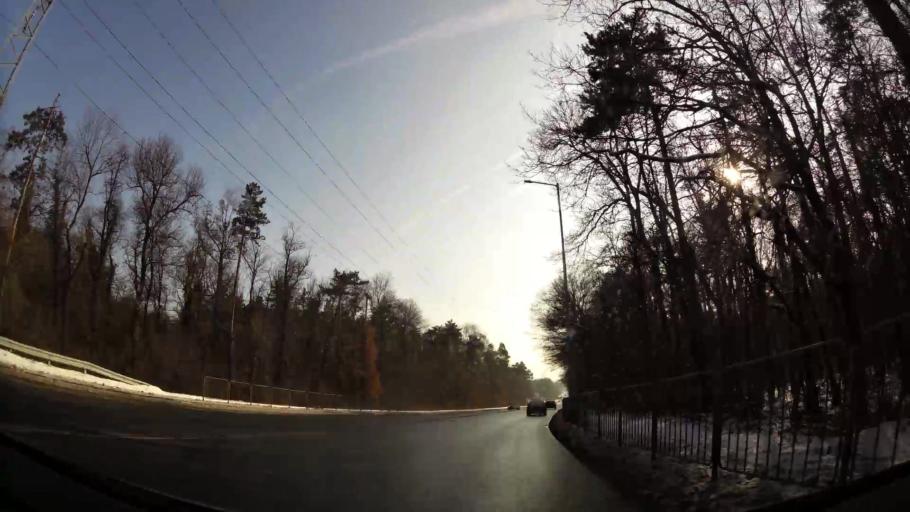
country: BG
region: Sofia-Capital
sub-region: Stolichna Obshtina
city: Sofia
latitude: 42.6704
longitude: 23.3379
